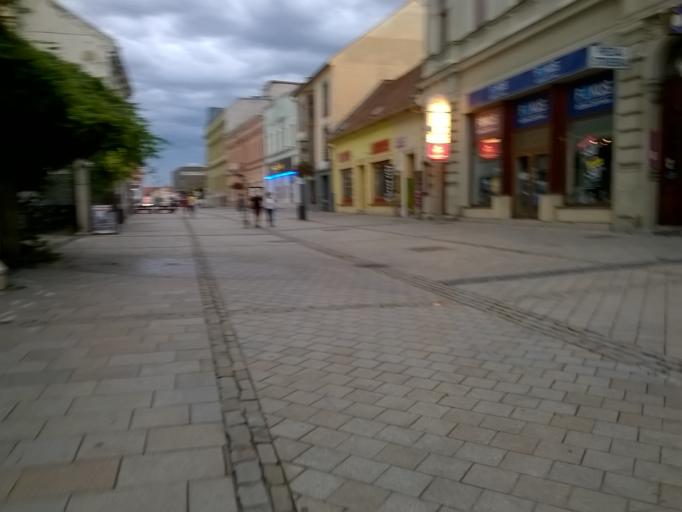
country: SK
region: Nitriansky
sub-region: Okres Nitra
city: Nitra
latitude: 48.3111
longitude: 18.0868
